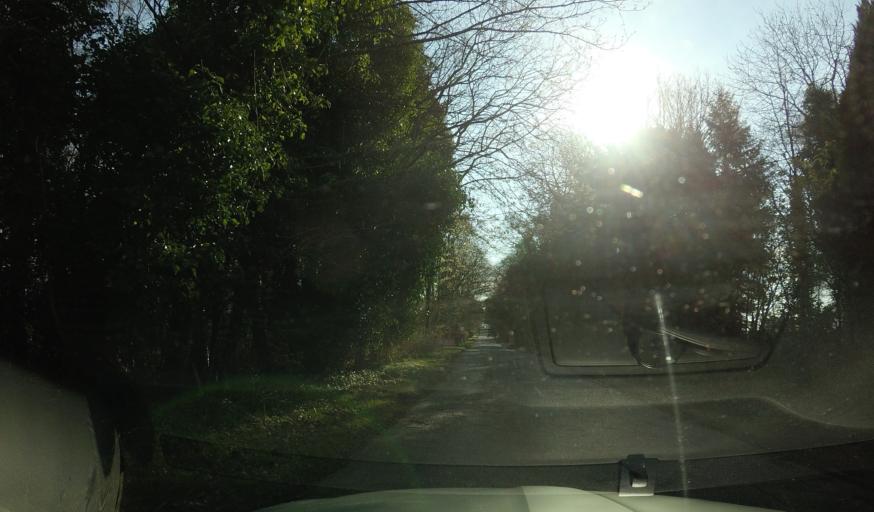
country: GB
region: Scotland
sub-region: Midlothian
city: Penicuik
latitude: 55.8478
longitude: -3.2245
